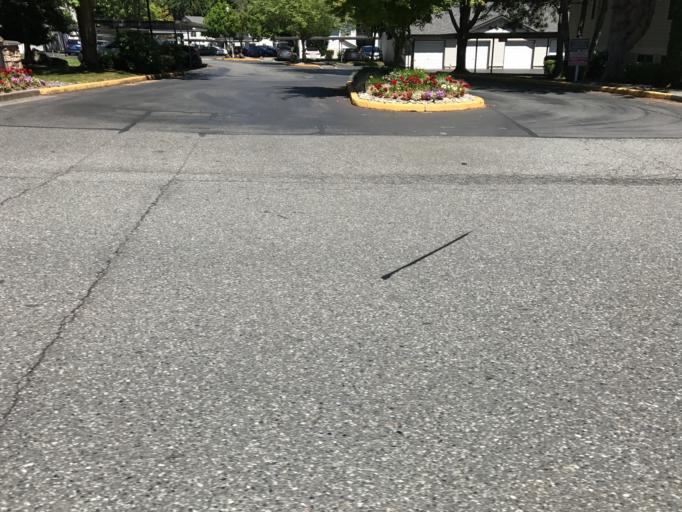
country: US
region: Washington
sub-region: King County
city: Redmond
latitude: 47.6460
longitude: -122.1306
